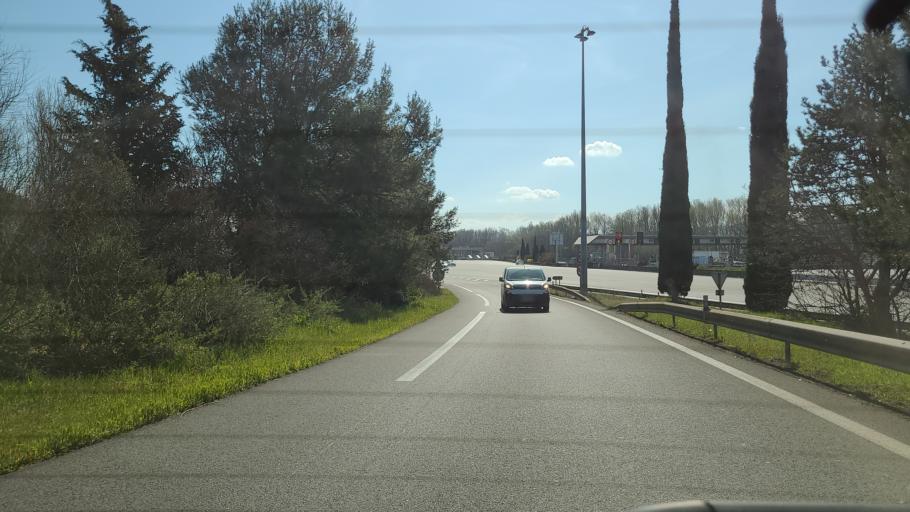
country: FR
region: Provence-Alpes-Cote d'Azur
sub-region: Departement des Bouches-du-Rhone
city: Chateauneuf-le-Rouge
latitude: 43.4845
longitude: 5.5372
